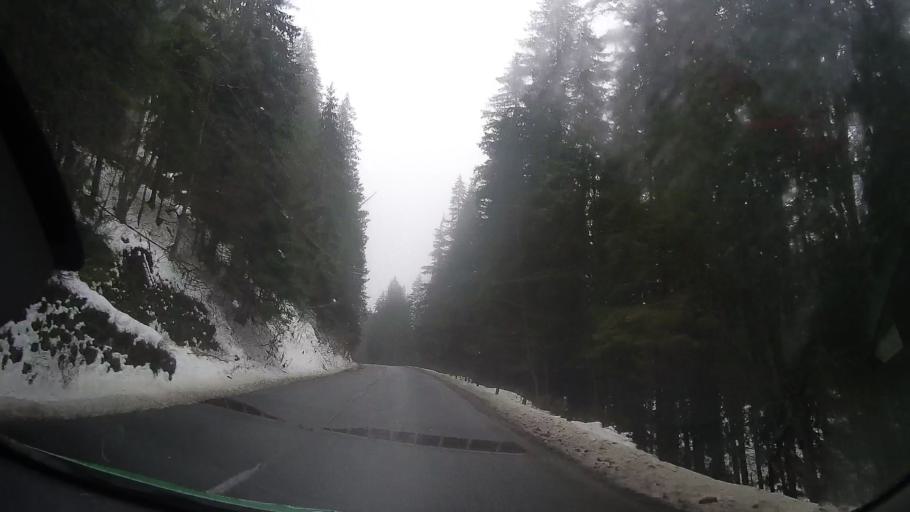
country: RO
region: Neamt
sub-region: Comuna Bicaz Chei
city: Bicaz Chei
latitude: 46.7873
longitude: 25.7880
